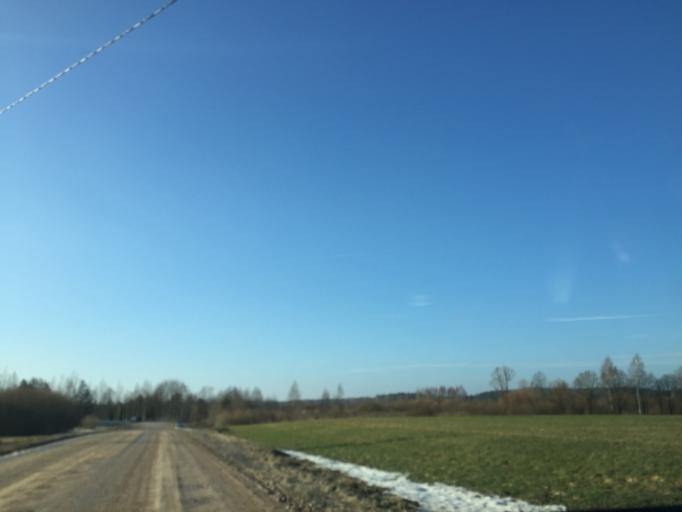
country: LV
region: Lecava
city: Iecava
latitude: 56.6828
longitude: 24.2319
